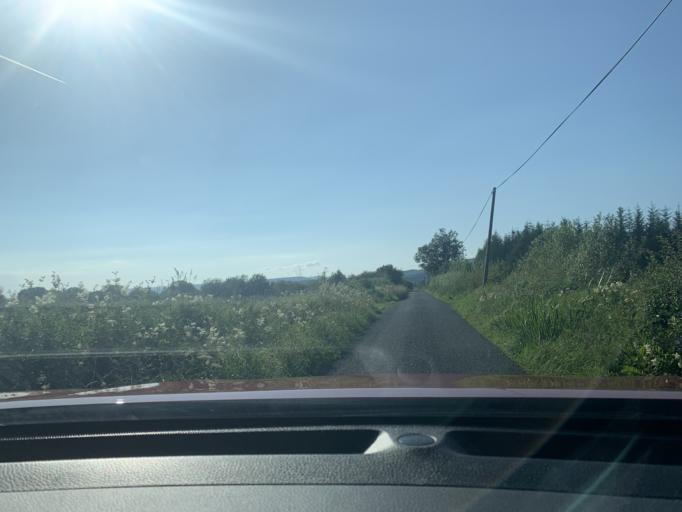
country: IE
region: Connaught
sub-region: Sligo
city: Tobercurry
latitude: 54.0753
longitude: -8.7852
